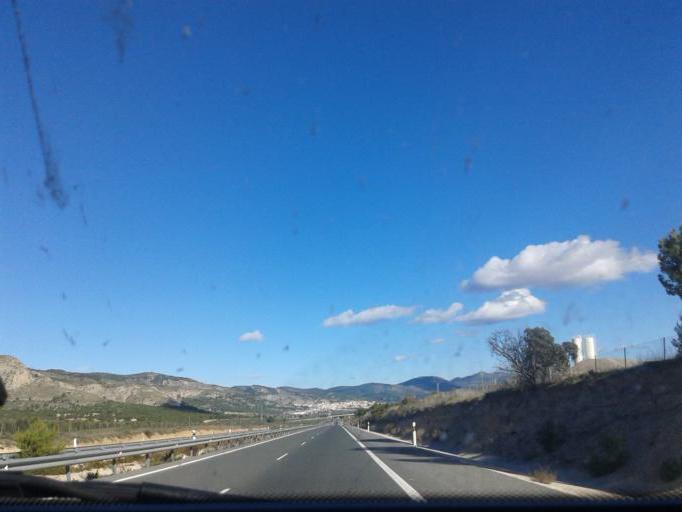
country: ES
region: Valencia
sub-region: Provincia de Alicante
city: Biar
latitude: 38.5970
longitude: -0.7303
